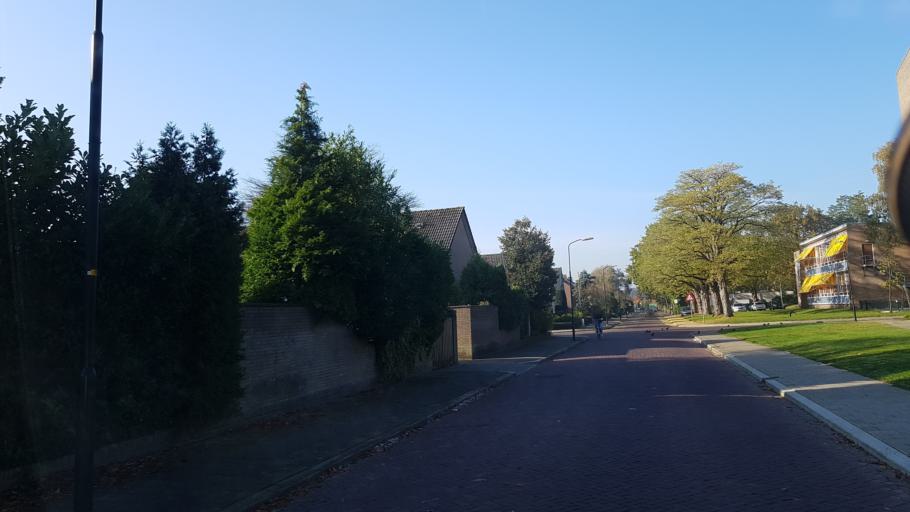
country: NL
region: Gelderland
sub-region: Gemeente Apeldoorn
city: Apeldoorn
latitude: 52.2335
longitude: 5.9671
